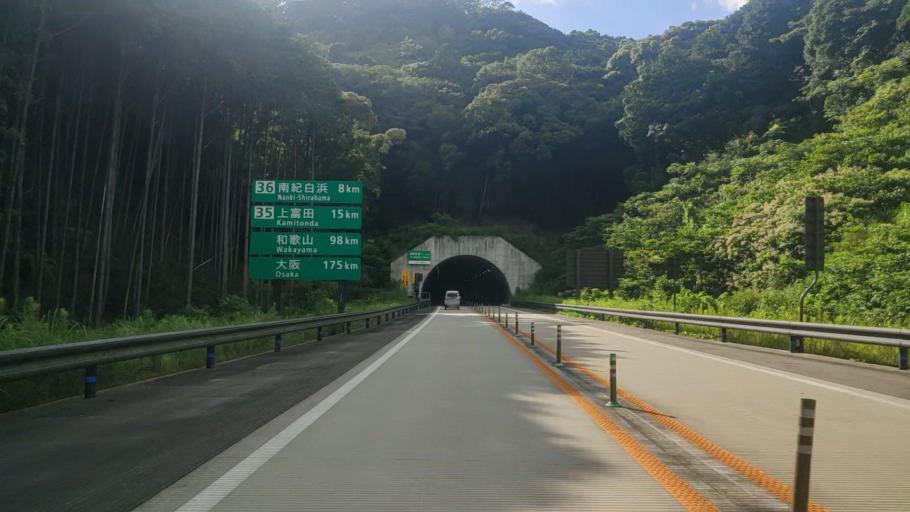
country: JP
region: Wakayama
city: Tanabe
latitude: 33.5860
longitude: 135.4470
